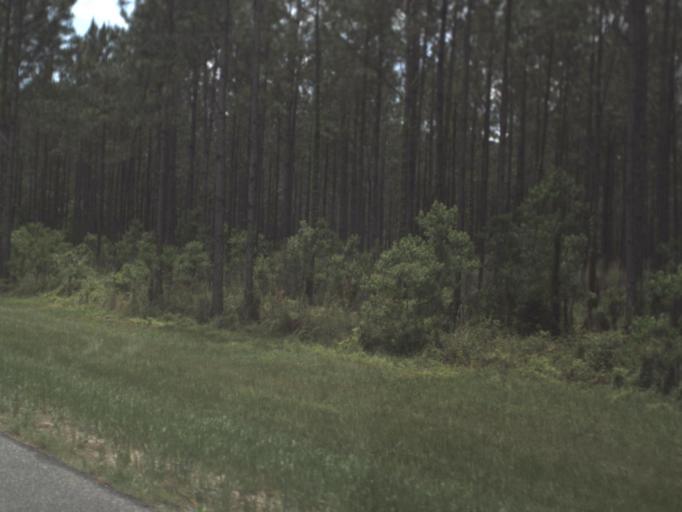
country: US
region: Florida
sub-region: Calhoun County
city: Blountstown
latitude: 30.4009
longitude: -85.0871
